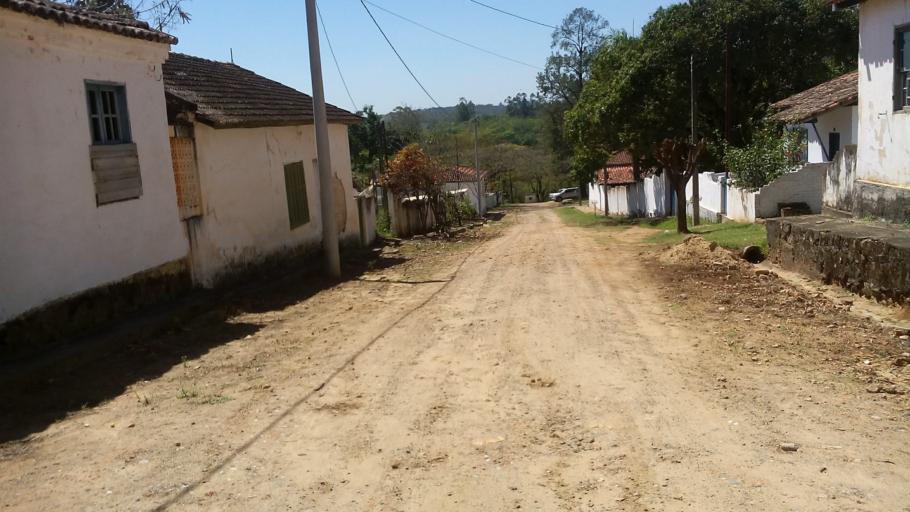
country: BR
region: Sao Paulo
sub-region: Aracoiaba Da Serra
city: Aracoiaba da Serra
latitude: -23.4258
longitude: -47.5992
